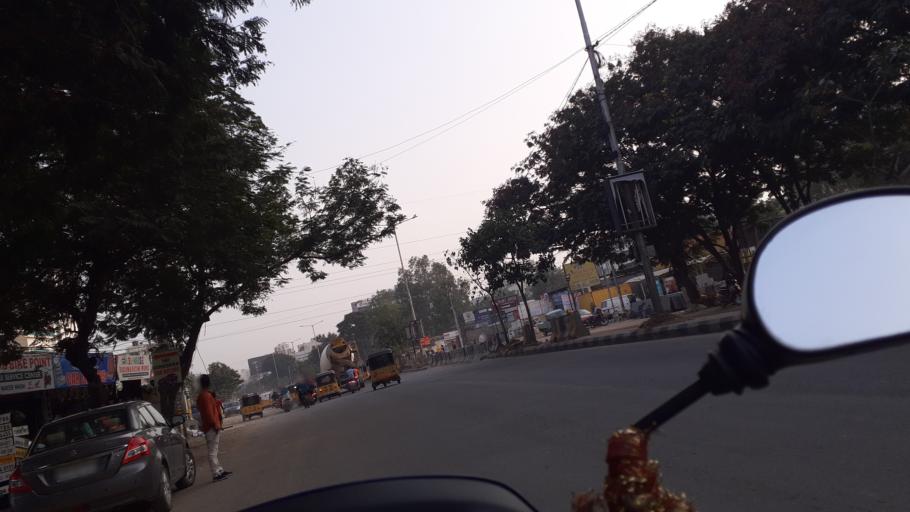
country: IN
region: Telangana
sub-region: Rangareddi
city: Kukatpalli
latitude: 17.4715
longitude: 78.3650
